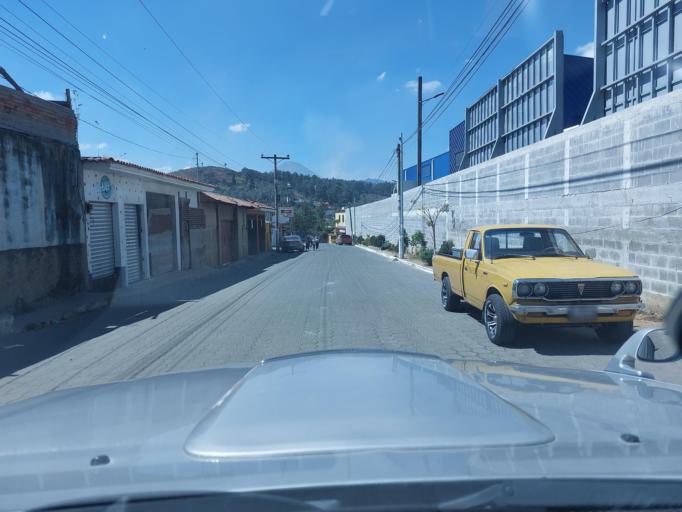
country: GT
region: Chimaltenango
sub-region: Municipio de Chimaltenango
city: Chimaltenango
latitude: 14.6592
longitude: -90.8288
